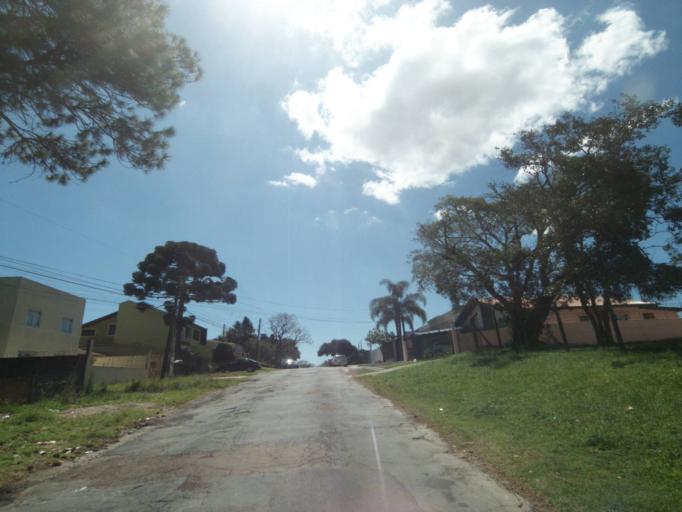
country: BR
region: Parana
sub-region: Curitiba
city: Curitiba
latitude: -25.3897
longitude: -49.2494
